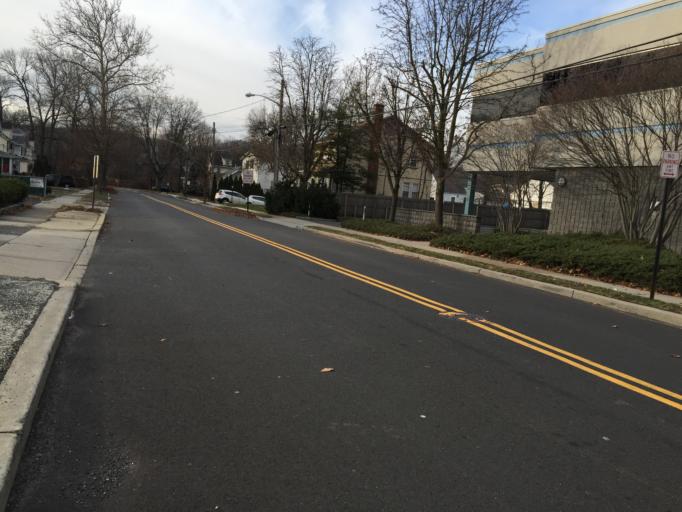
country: US
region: New Jersey
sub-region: Union County
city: Springfield
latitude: 40.7170
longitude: -74.3260
